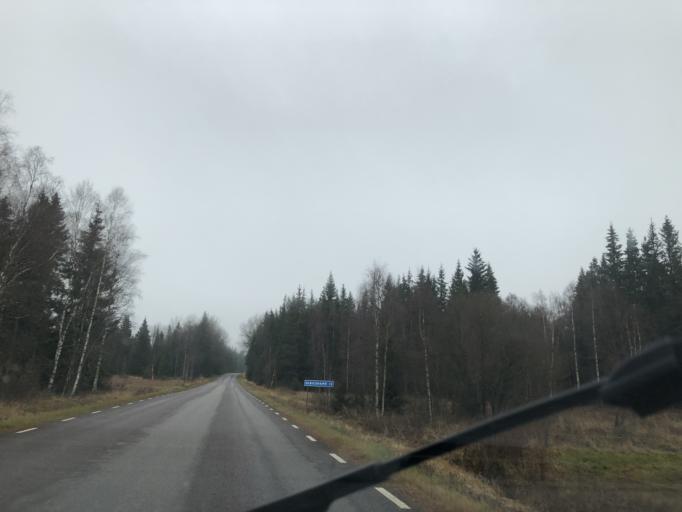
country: SE
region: Vaestra Goetaland
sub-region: Ulricehamns Kommun
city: Ulricehamn
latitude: 57.7263
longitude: 13.5484
